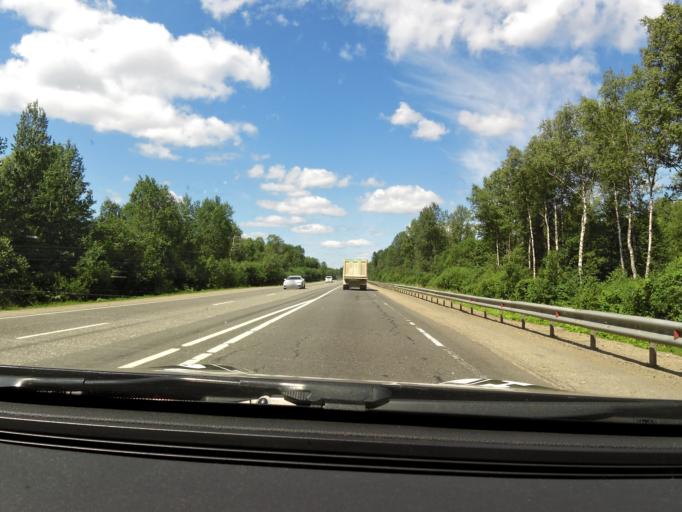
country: RU
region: Tverskaya
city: Vypolzovo
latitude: 57.8398
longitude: 33.7807
